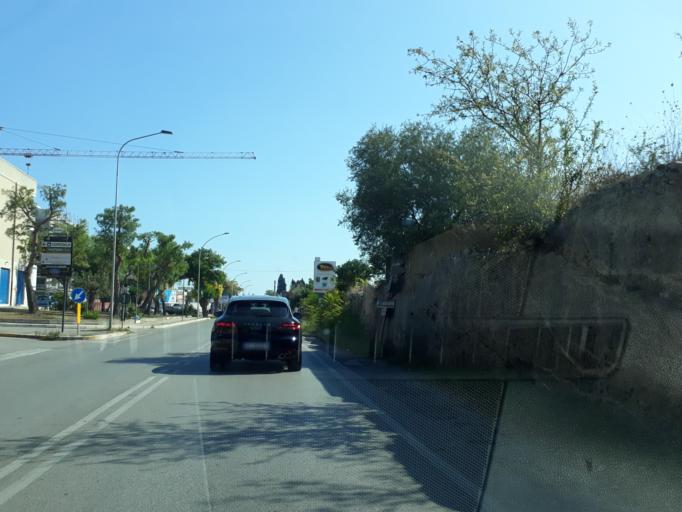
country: IT
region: Apulia
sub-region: Provincia di Bari
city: Monopoli
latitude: 40.9456
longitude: 17.2958
